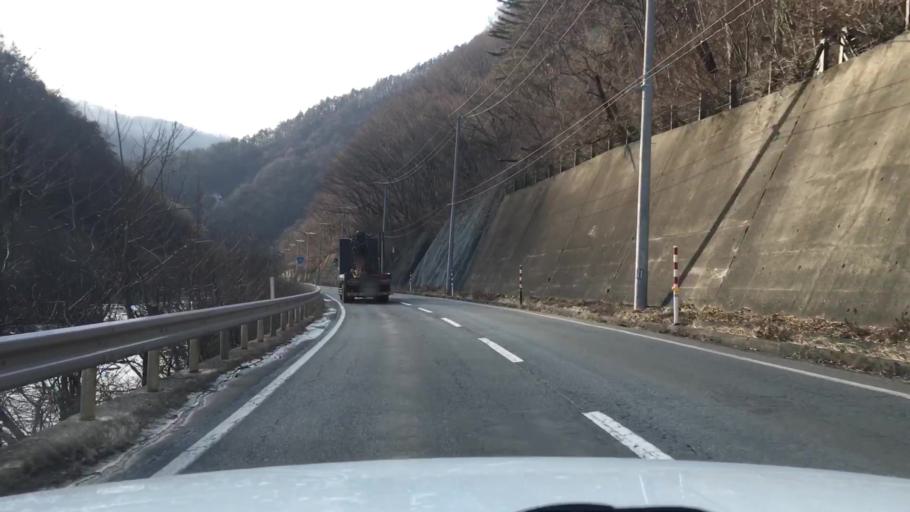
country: JP
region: Iwate
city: Tono
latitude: 39.6495
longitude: 141.5783
